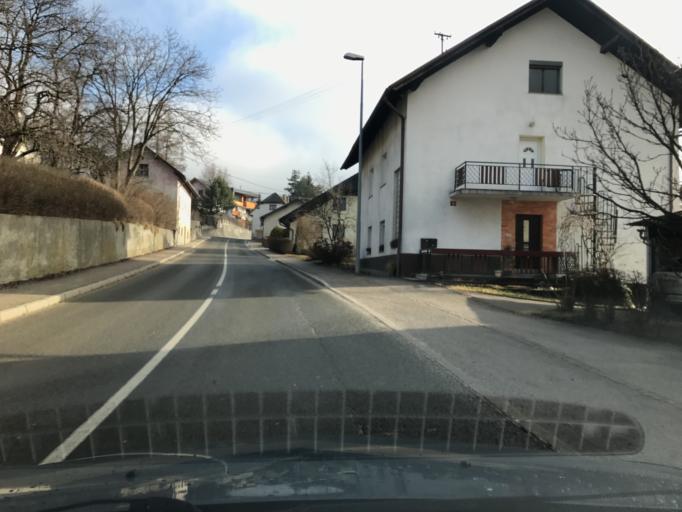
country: SI
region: Moravce
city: Moravce
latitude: 46.2184
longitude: 14.7591
